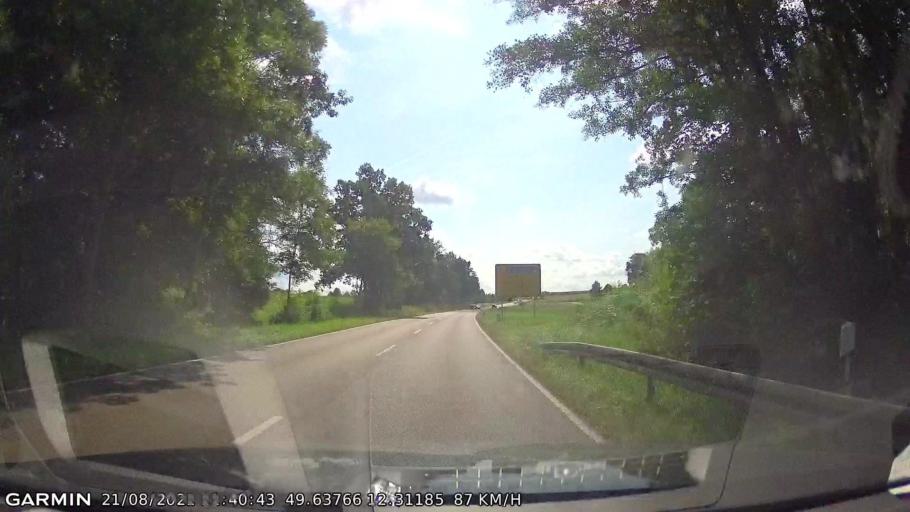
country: DE
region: Bavaria
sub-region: Upper Palatinate
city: Vohenstrauss
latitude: 49.6377
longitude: 12.3118
